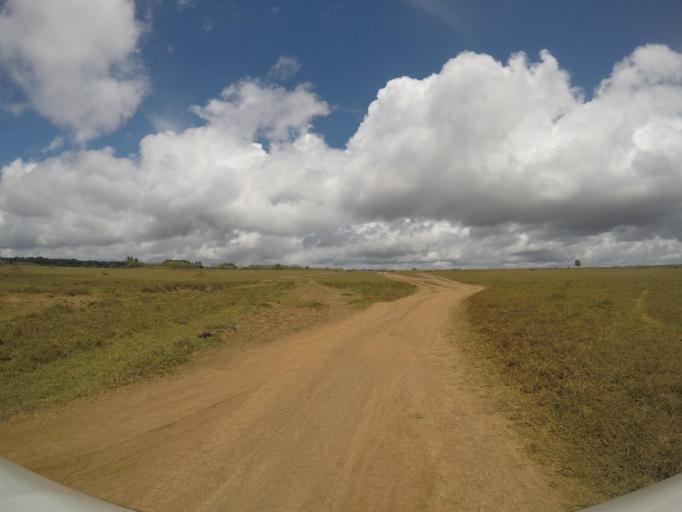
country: TL
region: Lautem
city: Lospalos
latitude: -8.4647
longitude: 126.9851
